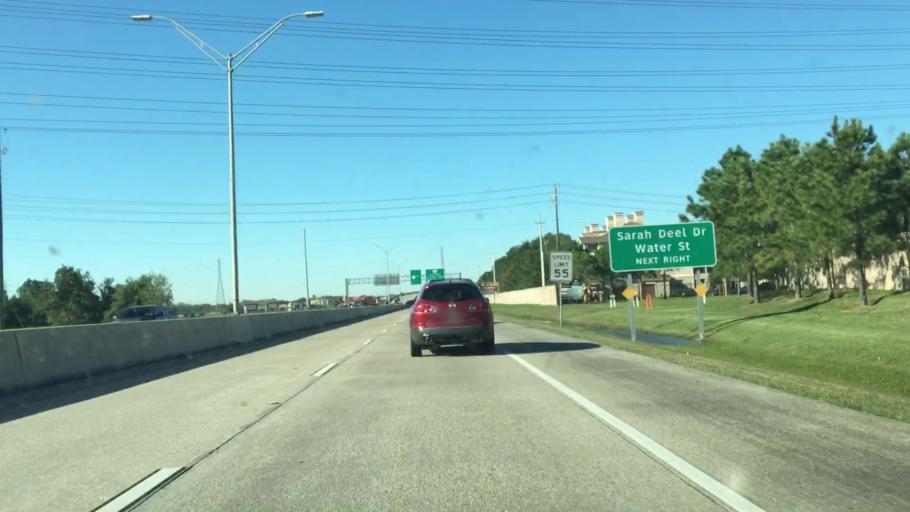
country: US
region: Texas
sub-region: Harris County
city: Webster
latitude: 29.5354
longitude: -95.1102
